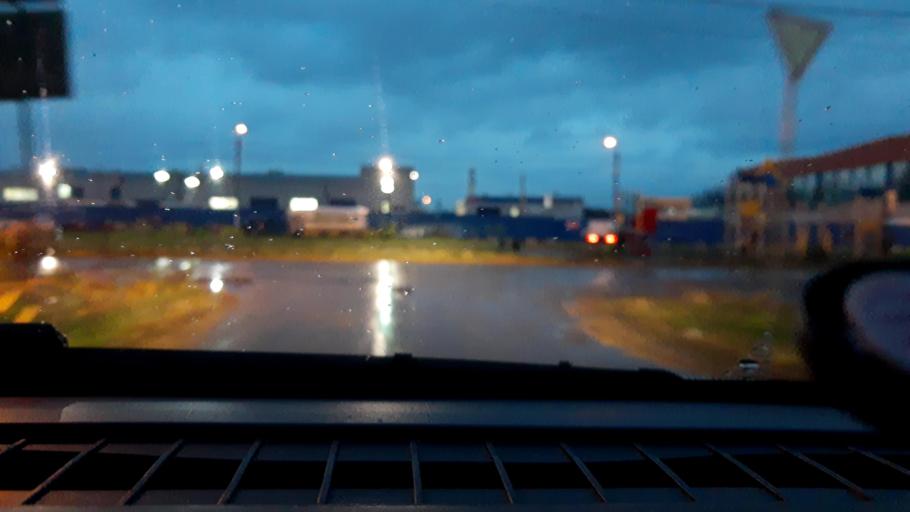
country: RU
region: Nizjnij Novgorod
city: Afonino
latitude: 56.2067
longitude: 44.1083
